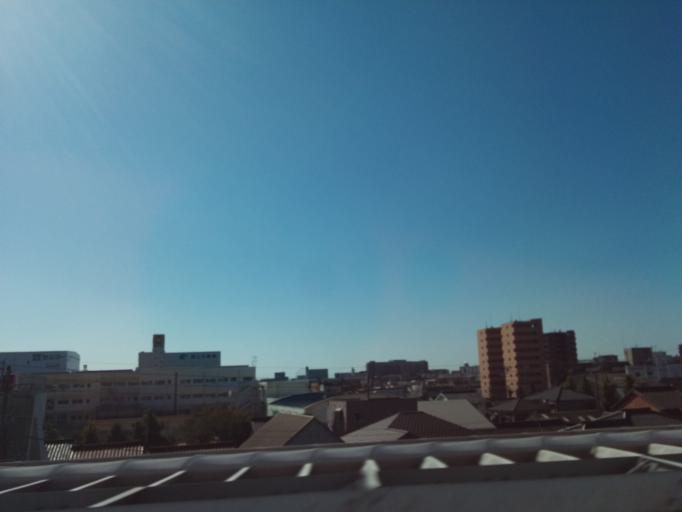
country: JP
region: Aichi
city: Nagoya-shi
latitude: 35.1148
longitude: 136.8977
